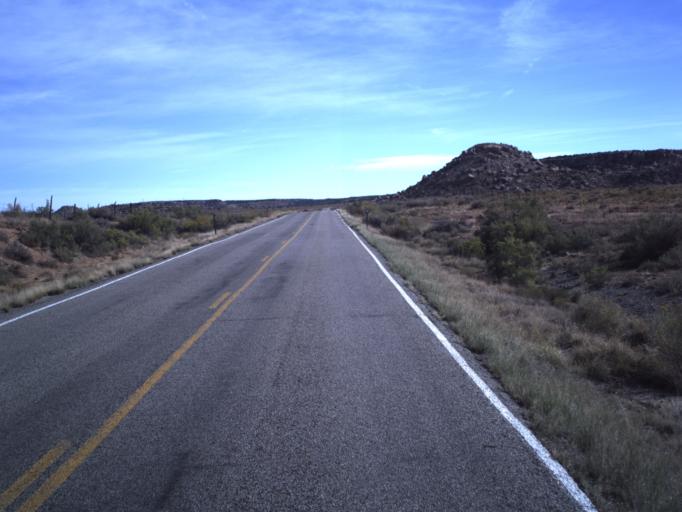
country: US
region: Utah
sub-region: San Juan County
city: Blanding
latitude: 37.4216
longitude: -109.4198
